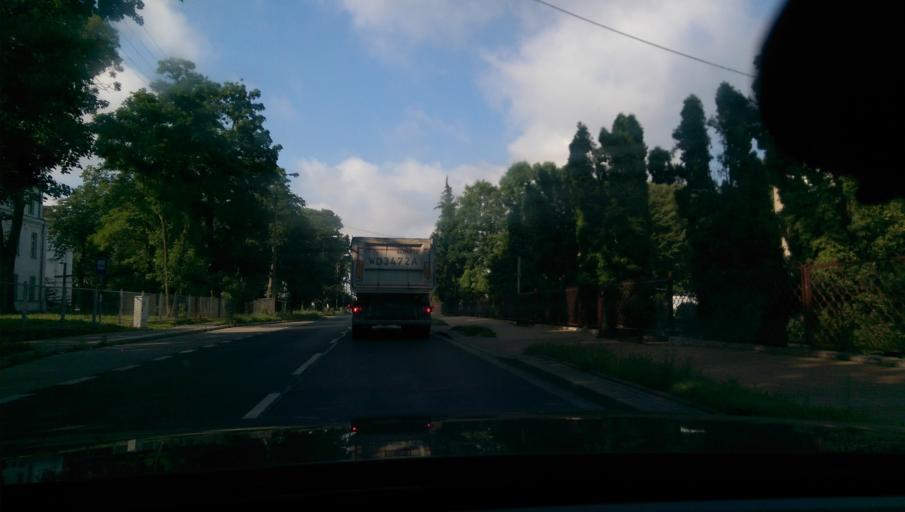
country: PL
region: Masovian Voivodeship
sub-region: Powiat ciechanowski
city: Ciechanow
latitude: 52.8897
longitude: 20.6296
